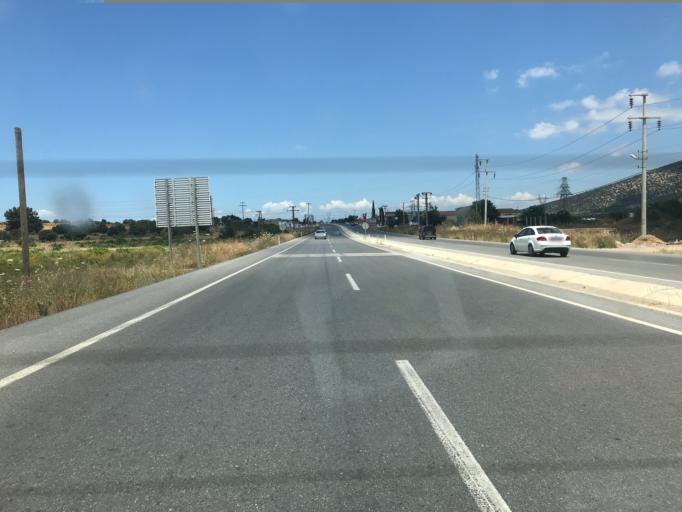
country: TR
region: Aydin
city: Akkoy
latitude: 37.4267
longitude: 27.3691
